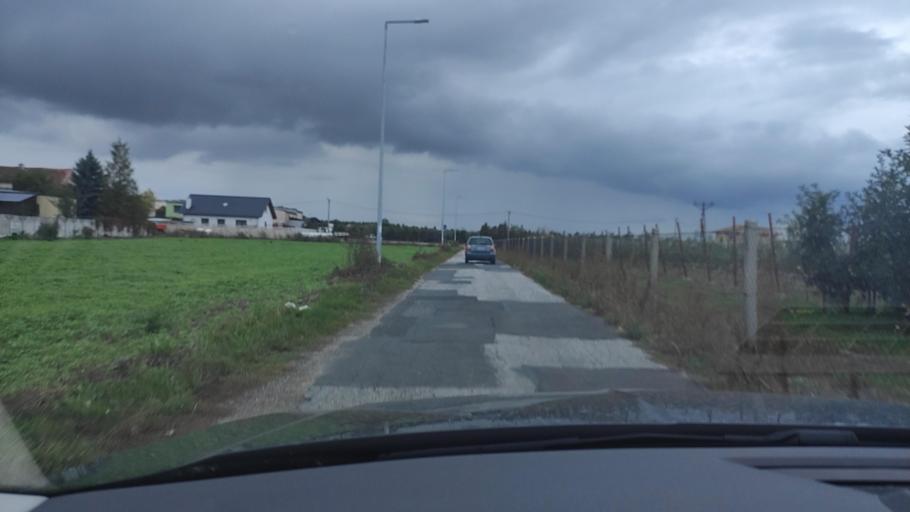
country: PL
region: Greater Poland Voivodeship
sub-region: Powiat poznanski
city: Kostrzyn
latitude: 52.3980
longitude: 17.1799
